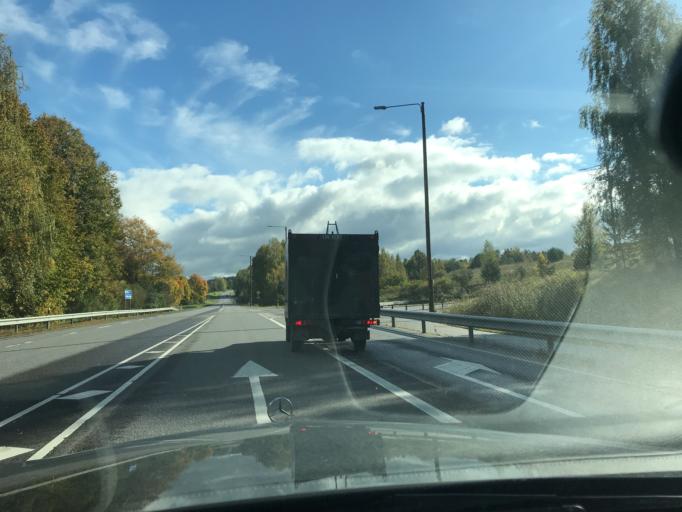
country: EE
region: Vorumaa
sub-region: Voru linn
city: Voru
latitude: 57.8091
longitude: 27.0661
